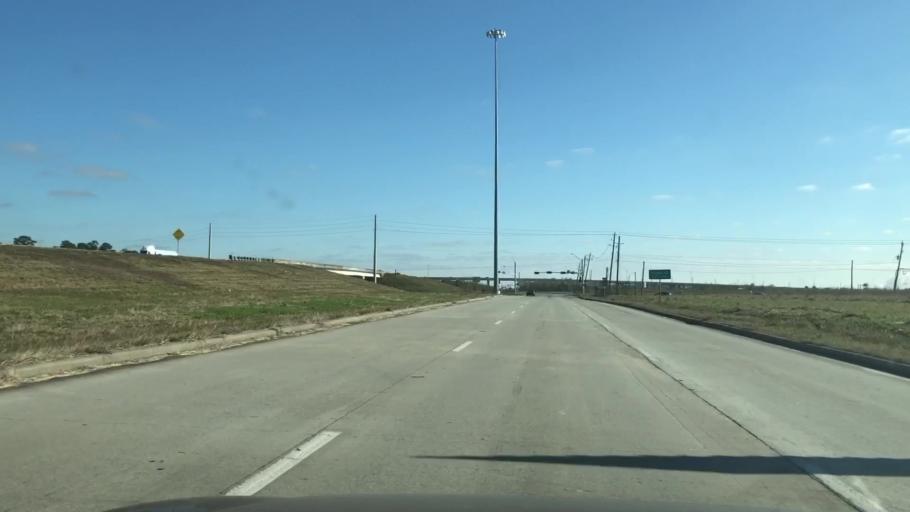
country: US
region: Texas
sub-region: Harris County
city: Cloverleaf
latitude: 29.8280
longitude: -95.1846
